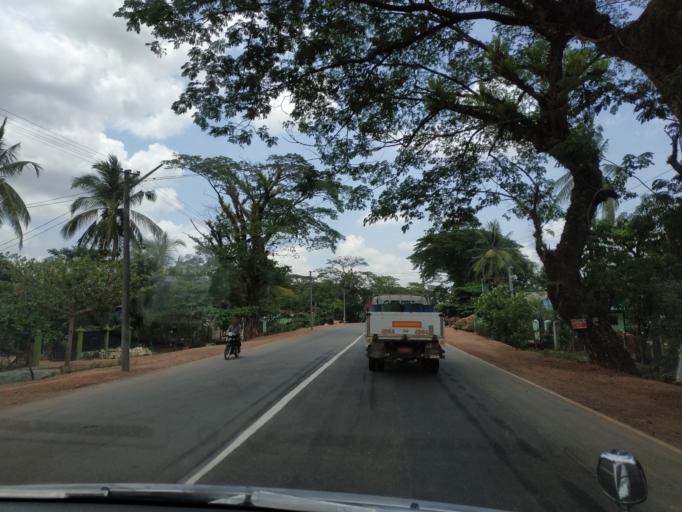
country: MM
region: Bago
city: Bago
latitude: 17.4668
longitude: 96.5832
